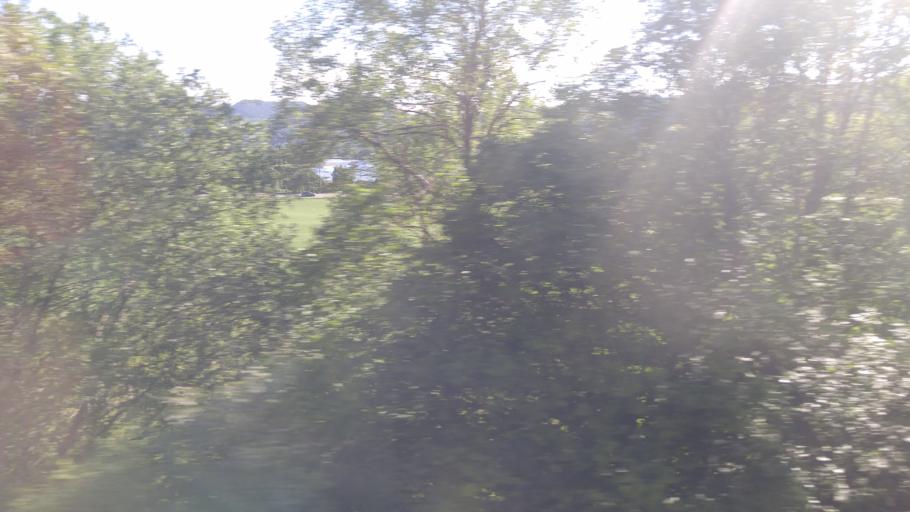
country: NO
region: Sor-Trondelag
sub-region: Melhus
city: Melhus
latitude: 63.2231
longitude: 10.2971
